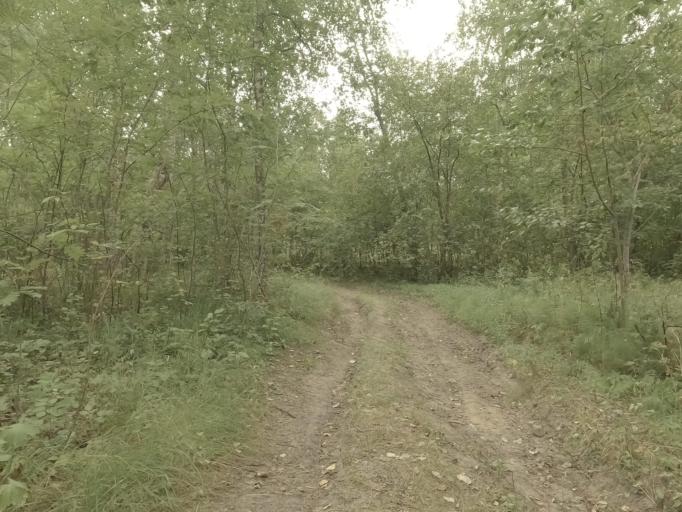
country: RU
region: Leningrad
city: Kamennogorsk
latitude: 61.0745
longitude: 29.1572
